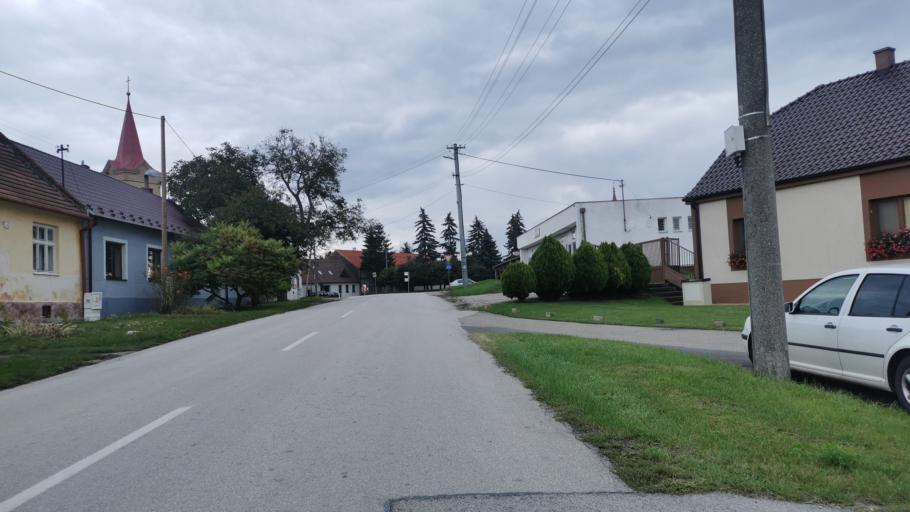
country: SK
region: Trnavsky
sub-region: Okres Skalica
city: Holic
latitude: 48.8245
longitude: 17.1903
